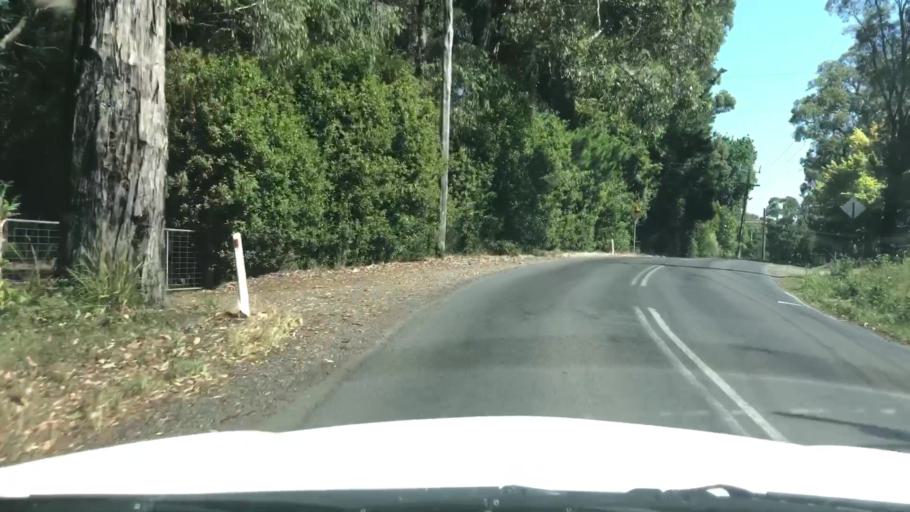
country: AU
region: Victoria
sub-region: Cardinia
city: Cockatoo
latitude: -37.9162
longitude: 145.4705
